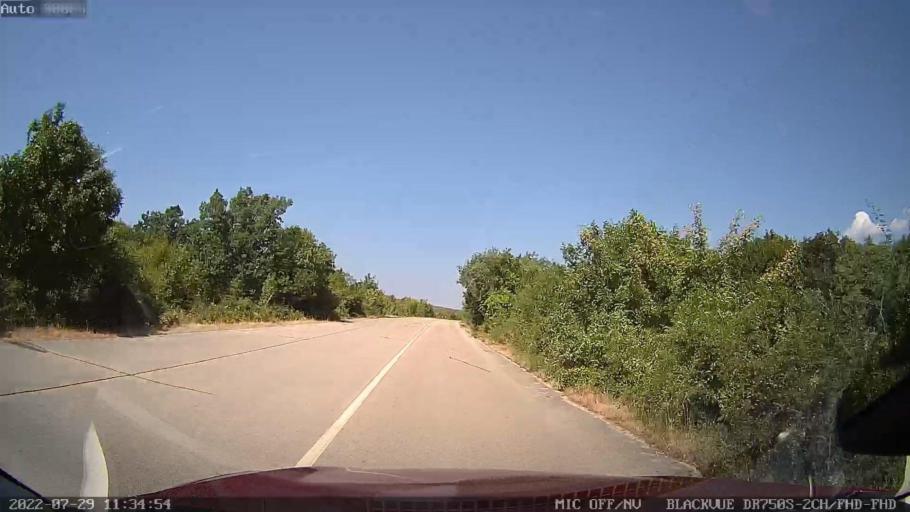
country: HR
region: Zadarska
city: Obrovac
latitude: 44.1796
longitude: 15.7214
